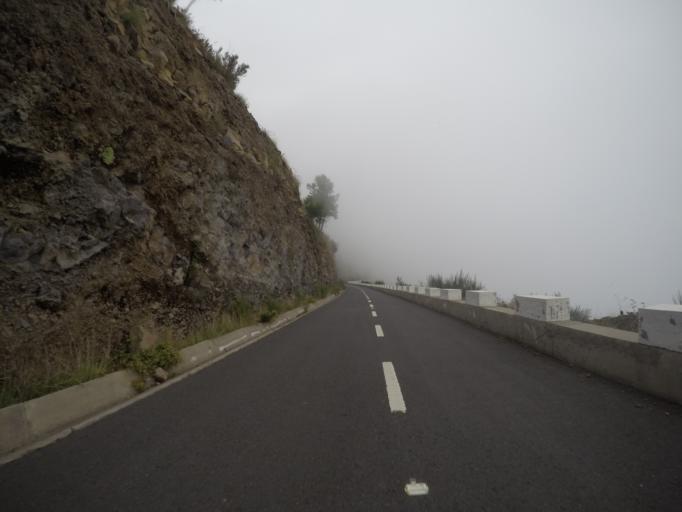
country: PT
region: Madeira
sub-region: Camara de Lobos
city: Curral das Freiras
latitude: 32.7076
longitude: -16.9556
